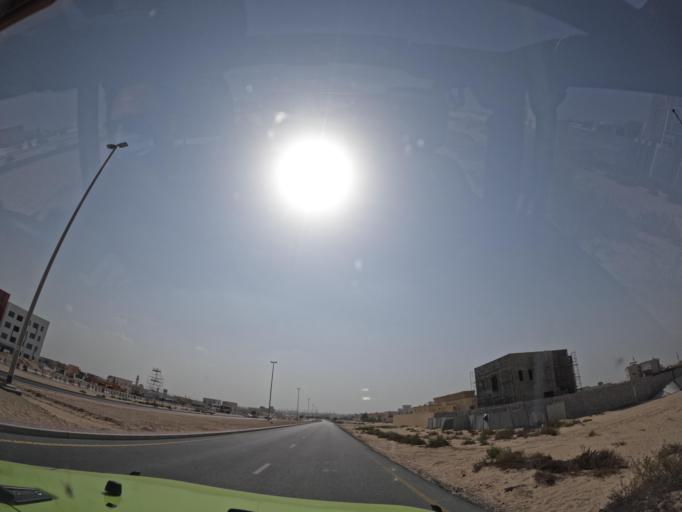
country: AE
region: Ash Shariqah
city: Sharjah
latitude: 25.1905
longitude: 55.4283
